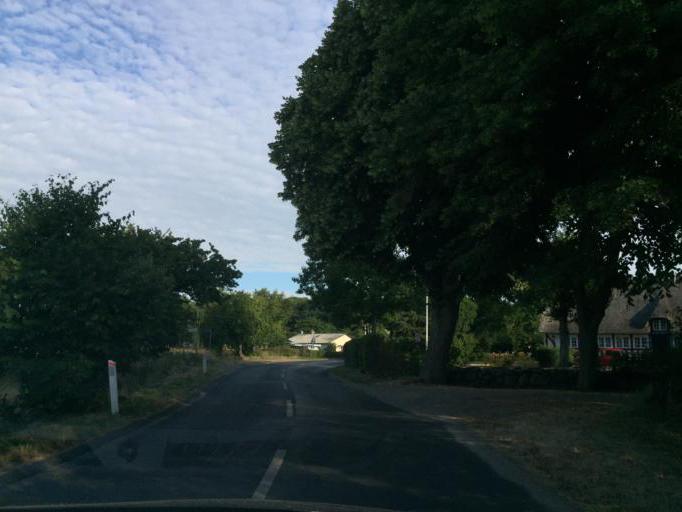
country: DK
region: South Denmark
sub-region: Assens Kommune
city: Harby
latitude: 55.1486
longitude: 10.0199
